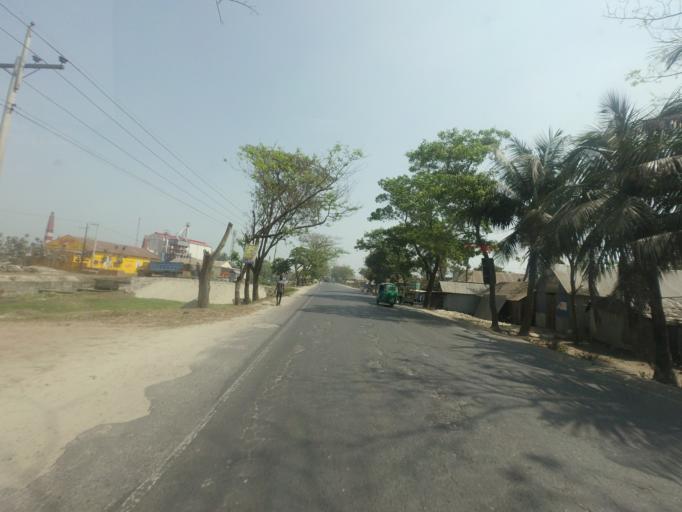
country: BD
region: Dhaka
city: Bhairab Bazar
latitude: 24.0413
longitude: 91.0424
